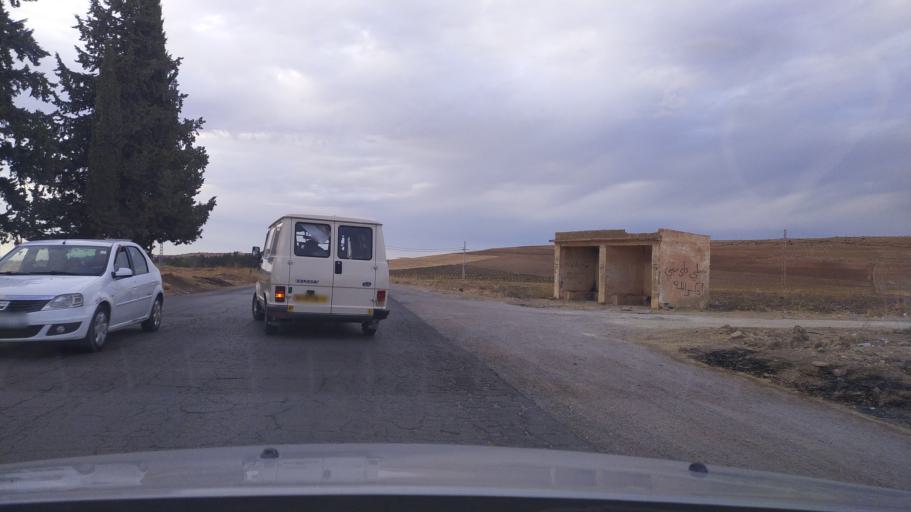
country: DZ
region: Tiaret
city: Frenda
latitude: 35.0267
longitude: 1.0983
